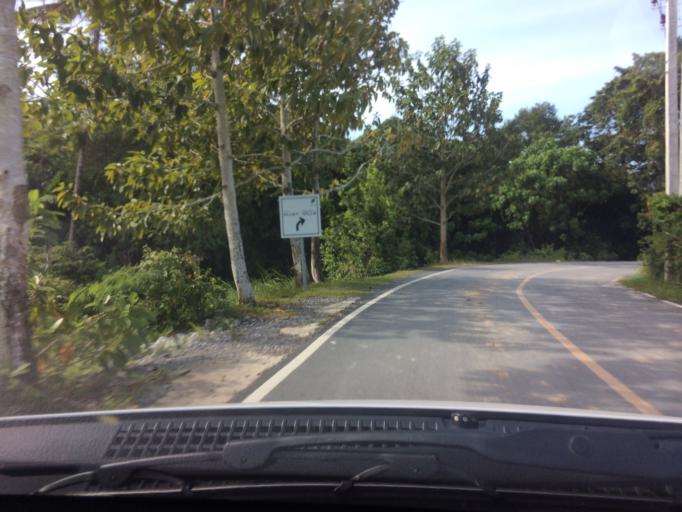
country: TH
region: Phuket
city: Thalang
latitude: 8.0430
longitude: 98.3278
